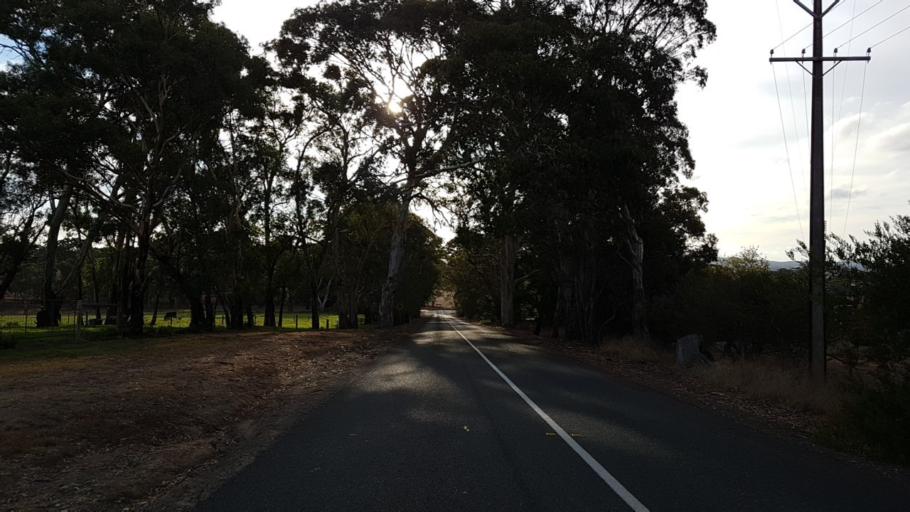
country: AU
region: South Australia
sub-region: Mount Barker
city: Nairne
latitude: -34.9932
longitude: 138.9046
